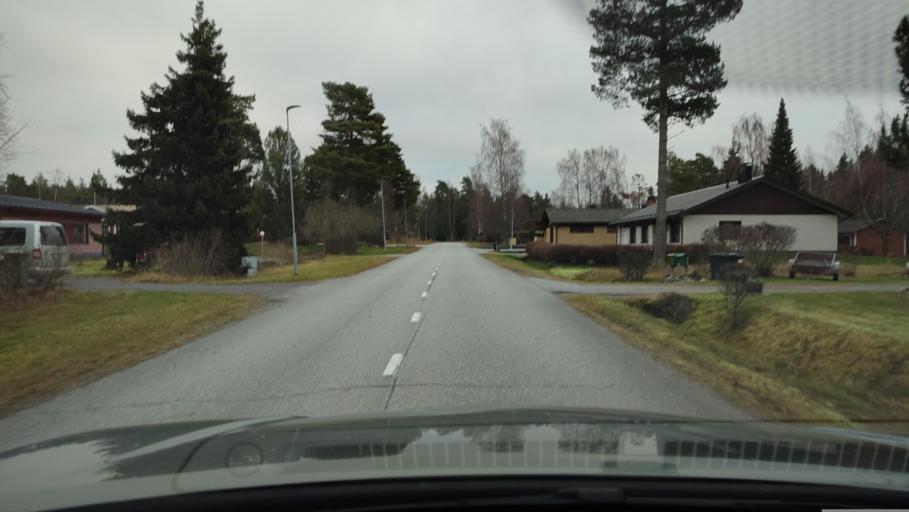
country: FI
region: Ostrobothnia
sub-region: Sydosterbotten
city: Kristinestad
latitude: 62.2668
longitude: 21.3936
